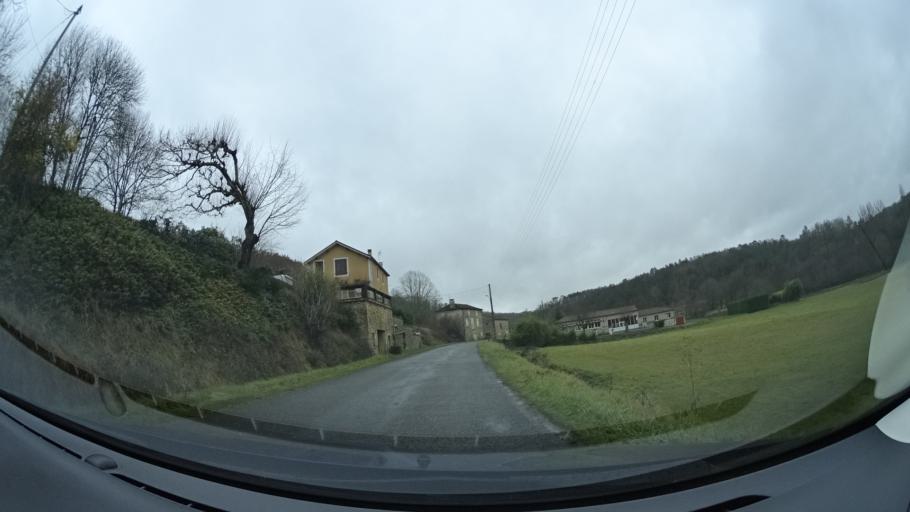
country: FR
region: Midi-Pyrenees
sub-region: Departement du Lot
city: Prayssac
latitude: 44.5397
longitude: 1.2330
